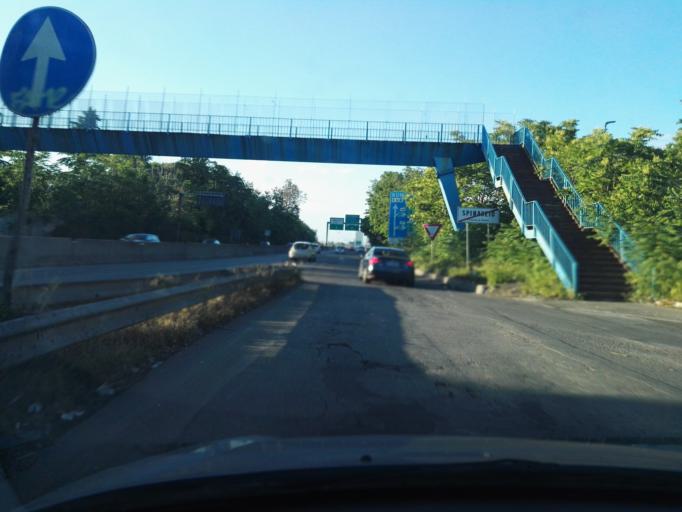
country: IT
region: Latium
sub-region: Citta metropolitana di Roma Capitale
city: Selcetta
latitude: 41.7961
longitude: 12.4529
